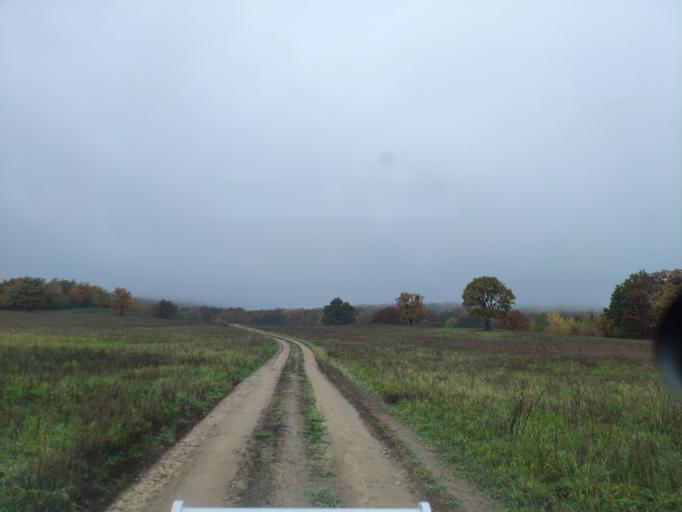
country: SK
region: Kosicky
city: Moldava nad Bodvou
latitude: 48.7123
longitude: 21.0145
